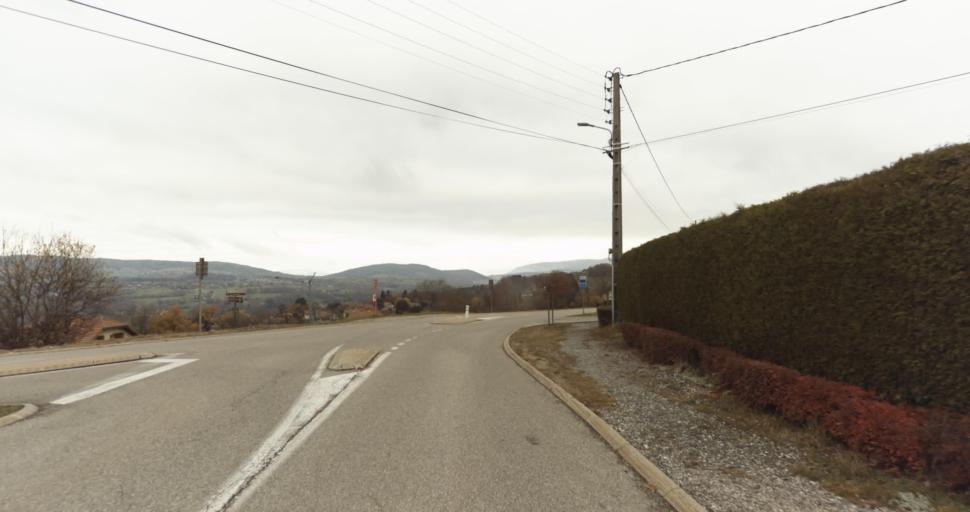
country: FR
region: Rhone-Alpes
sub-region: Departement de la Haute-Savoie
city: Saint-Martin-Bellevue
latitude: 45.9595
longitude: 6.1445
